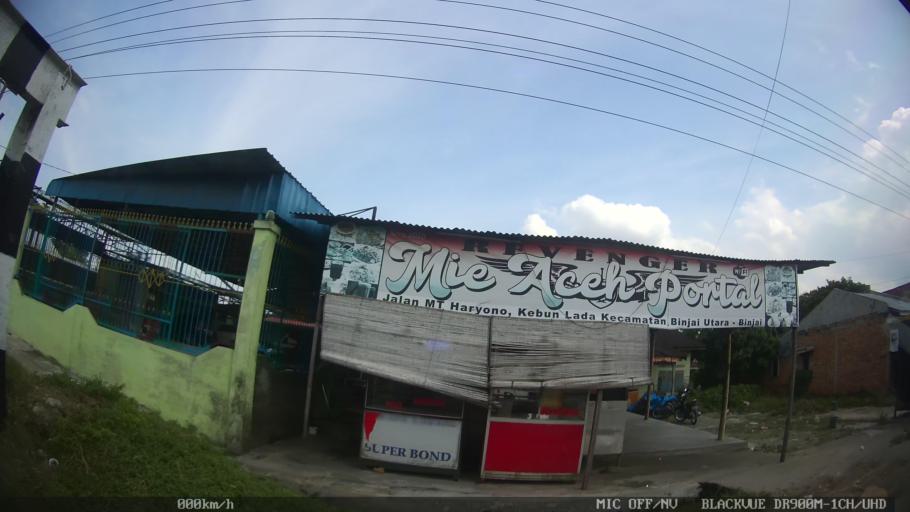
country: ID
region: North Sumatra
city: Binjai
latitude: 3.6358
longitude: 98.4905
